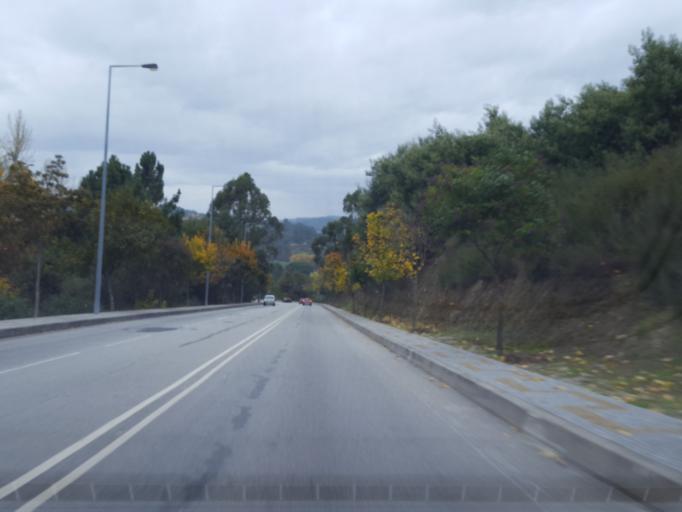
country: PT
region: Porto
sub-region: Marco de Canaveses
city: Marco de Canavezes
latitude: 41.1901
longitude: -8.1527
